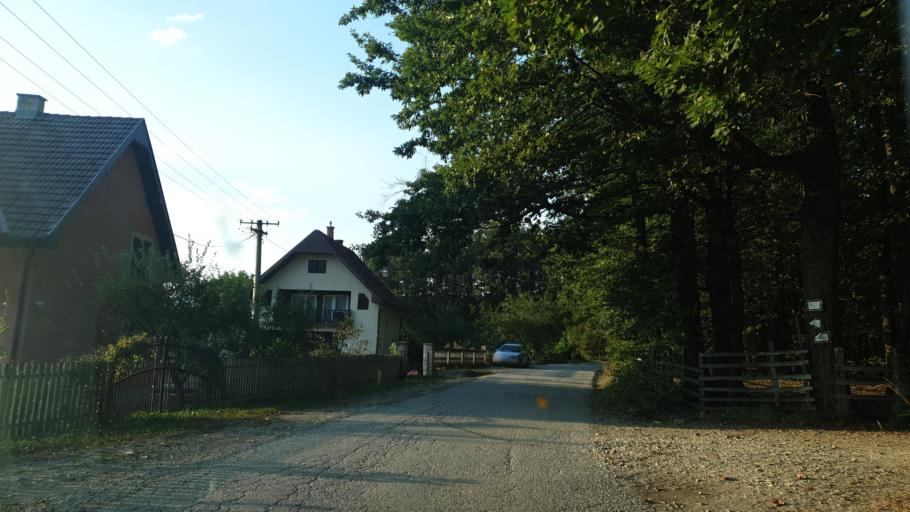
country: RS
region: Central Serbia
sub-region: Zlatiborski Okrug
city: Kosjeric
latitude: 43.9823
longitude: 20.0133
